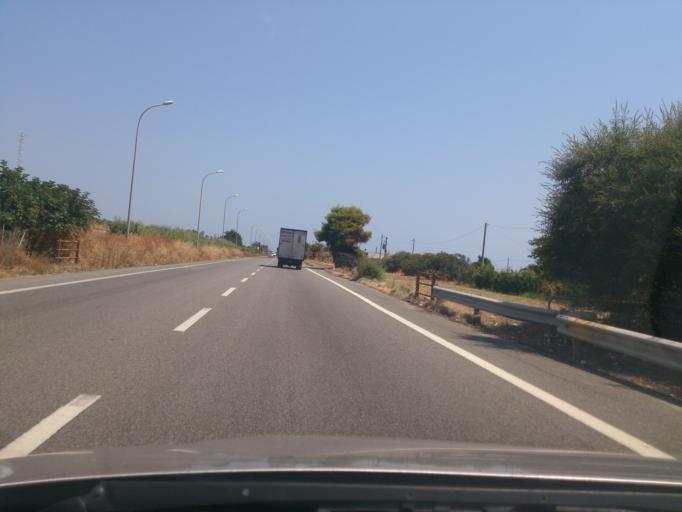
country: IT
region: Calabria
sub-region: Provincia di Reggio Calabria
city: Riace Marina
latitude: 38.4047
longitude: 16.5468
